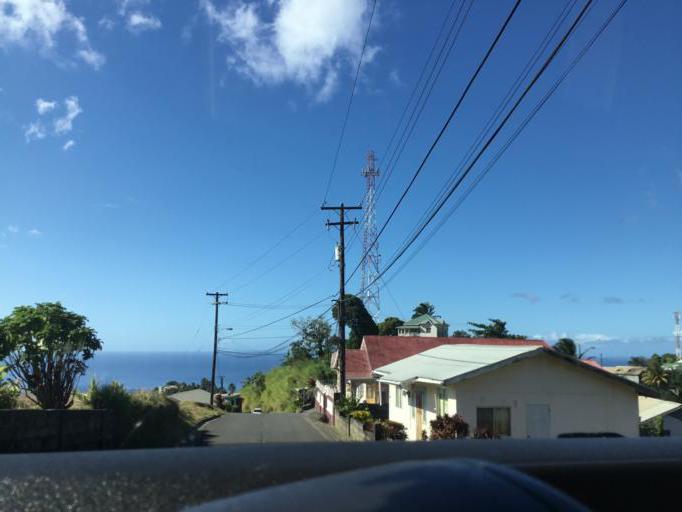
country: VC
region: Saint David
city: Chateaubelair
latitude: 13.2719
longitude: -61.2418
